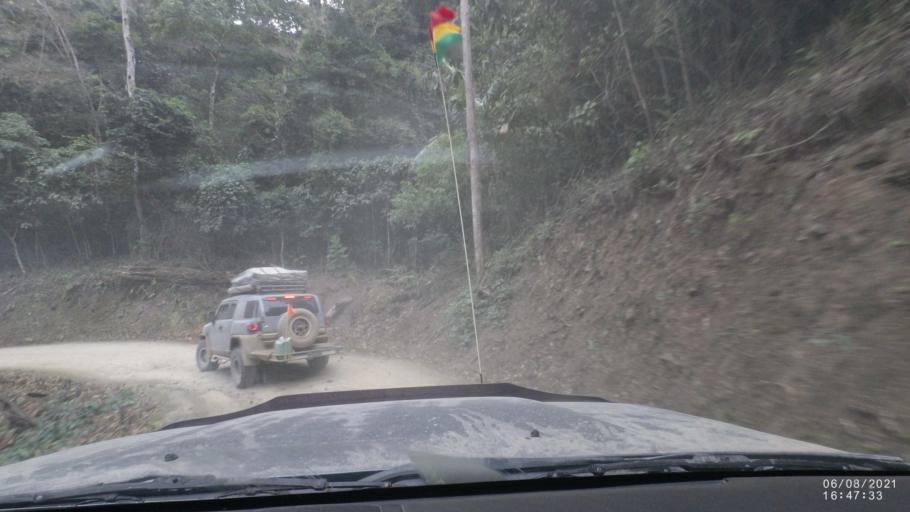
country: BO
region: La Paz
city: Quime
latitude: -16.5023
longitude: -66.7620
